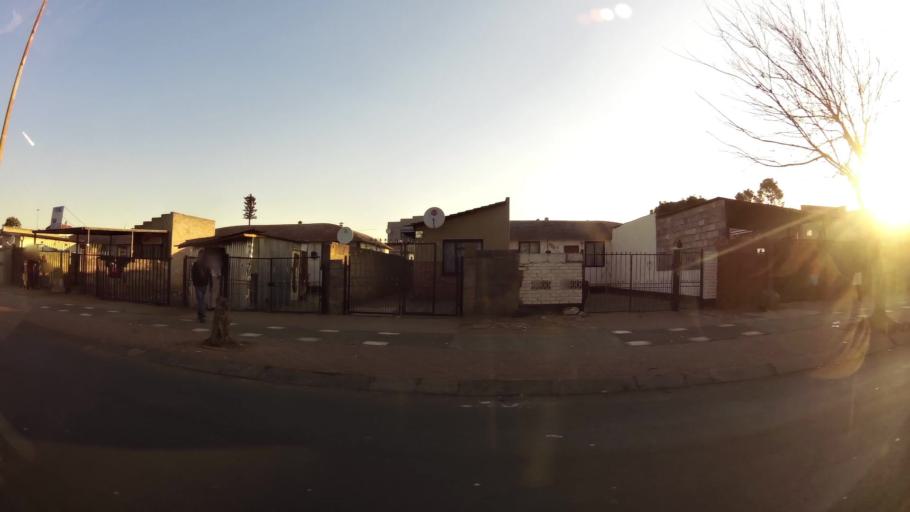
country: ZA
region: Gauteng
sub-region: City of Johannesburg Metropolitan Municipality
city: Soweto
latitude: -26.2467
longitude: 27.8825
